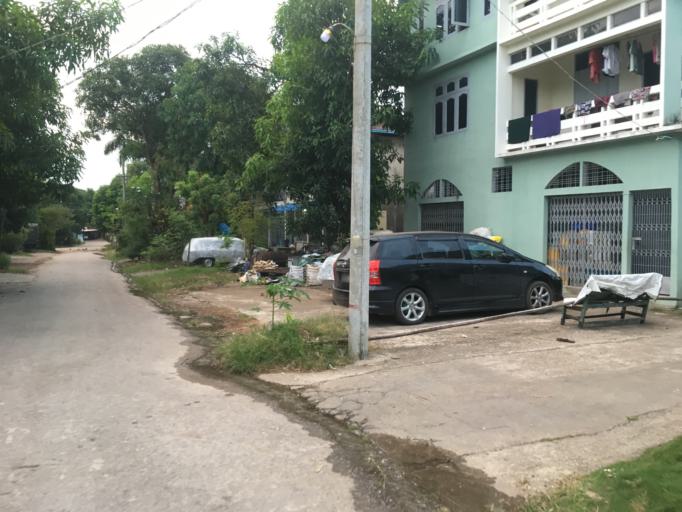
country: MM
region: Mon
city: Mawlamyine
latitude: 16.4765
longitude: 97.6215
